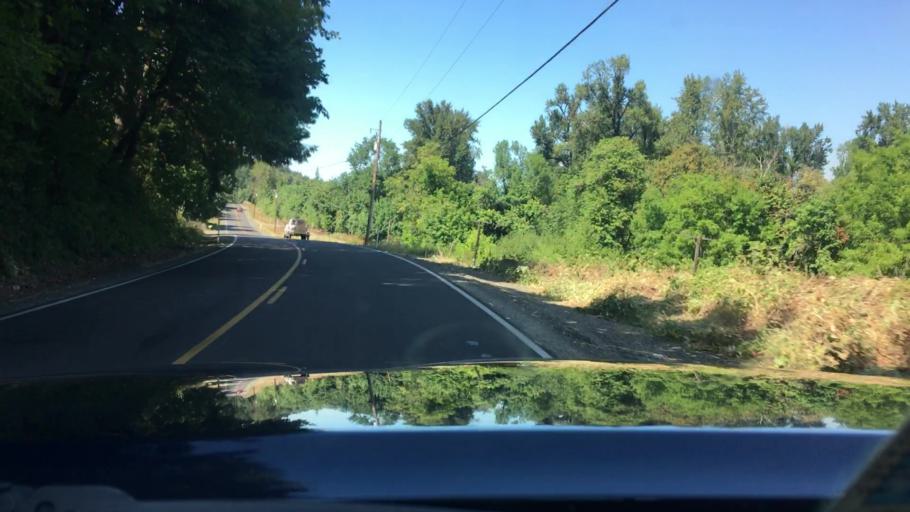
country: US
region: Oregon
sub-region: Lane County
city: Cottage Grove
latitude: 43.8147
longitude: -123.0457
